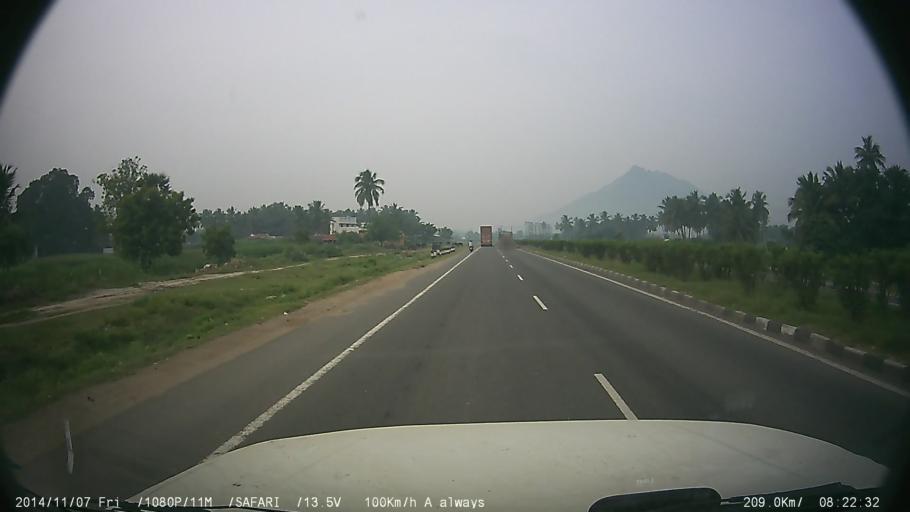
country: IN
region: Tamil Nadu
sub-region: Salem
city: Salem
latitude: 11.6268
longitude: 78.1134
